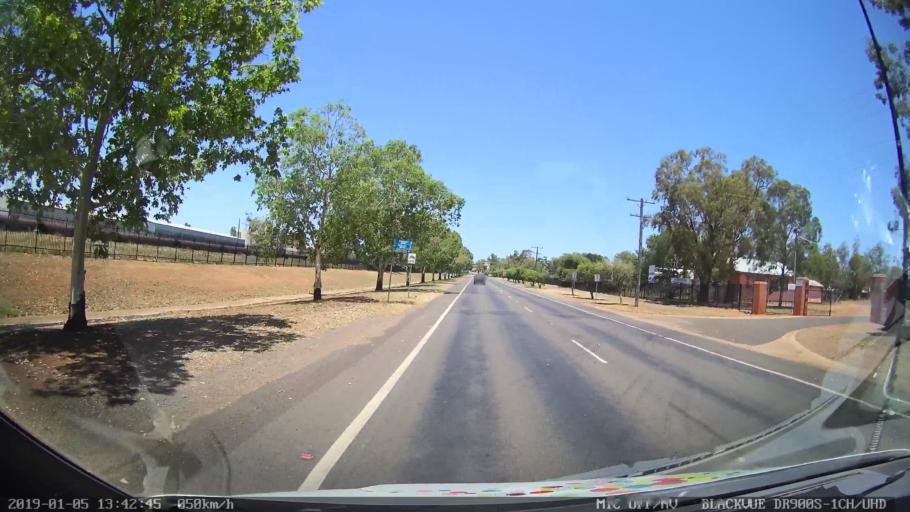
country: AU
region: New South Wales
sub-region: Gunnedah
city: Gunnedah
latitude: -30.9798
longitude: 150.2479
